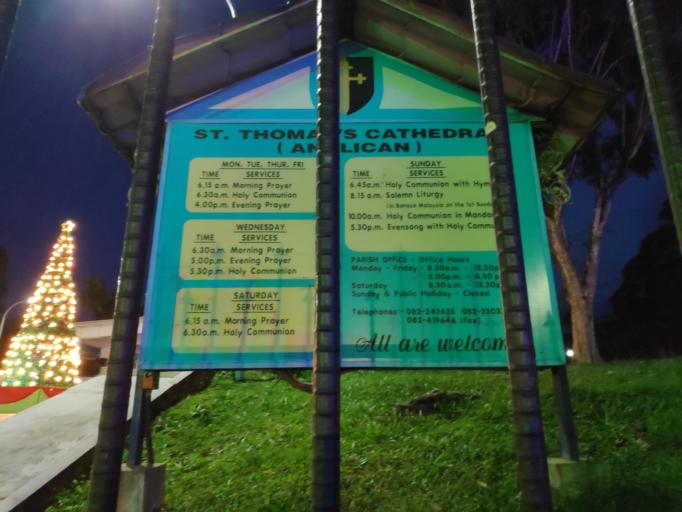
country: MY
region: Sarawak
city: Kuching
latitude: 1.5574
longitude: 110.3444
